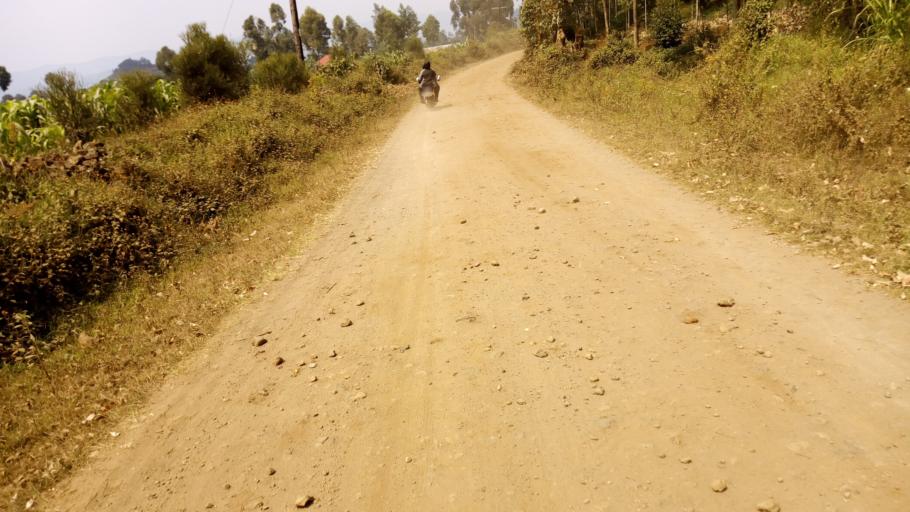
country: UG
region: Western Region
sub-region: Kisoro District
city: Kisoro
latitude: -1.3140
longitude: 29.7143
